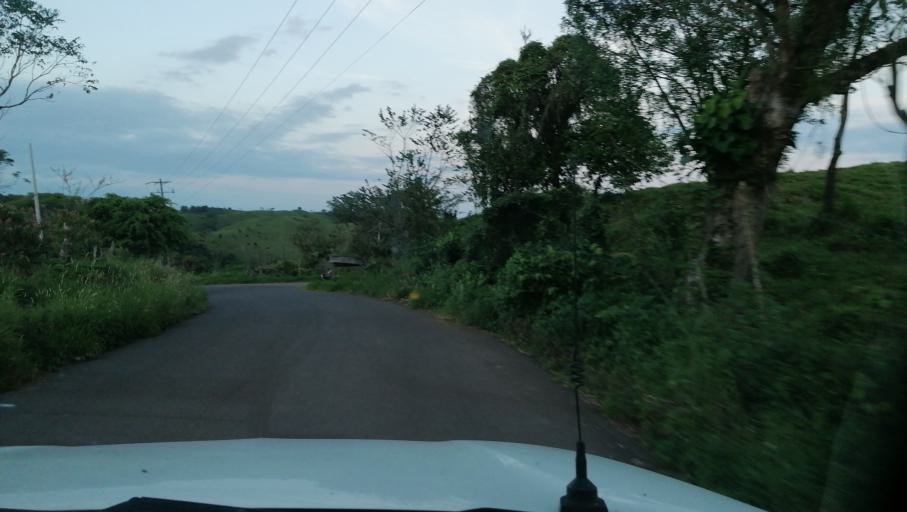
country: MX
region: Chiapas
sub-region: Ostuacan
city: Nuevo Juan del Grijalva
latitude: 17.4382
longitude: -93.3505
